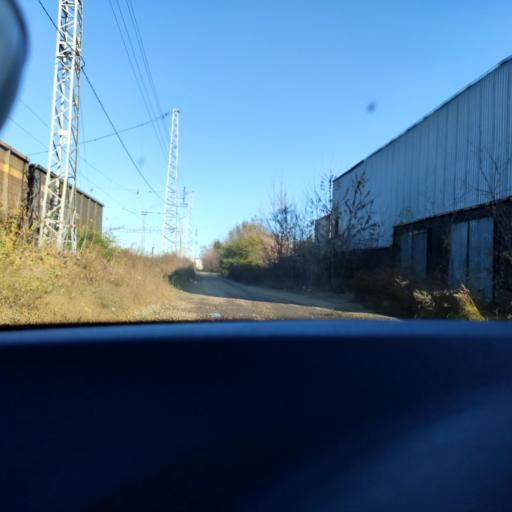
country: RU
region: Samara
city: Samara
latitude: 53.2070
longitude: 50.2568
